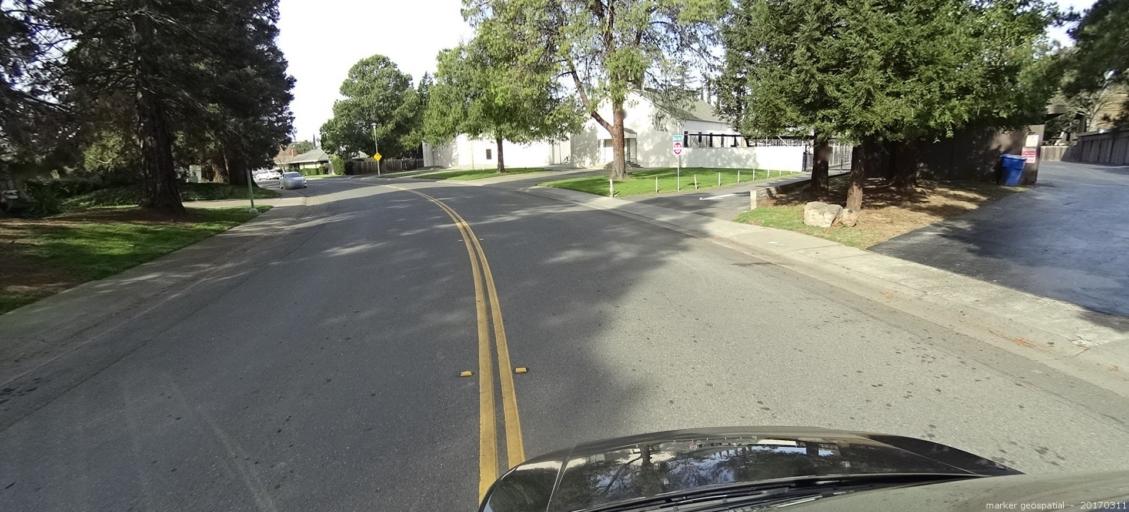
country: US
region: California
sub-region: Yolo County
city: West Sacramento
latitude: 38.5056
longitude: -121.5505
